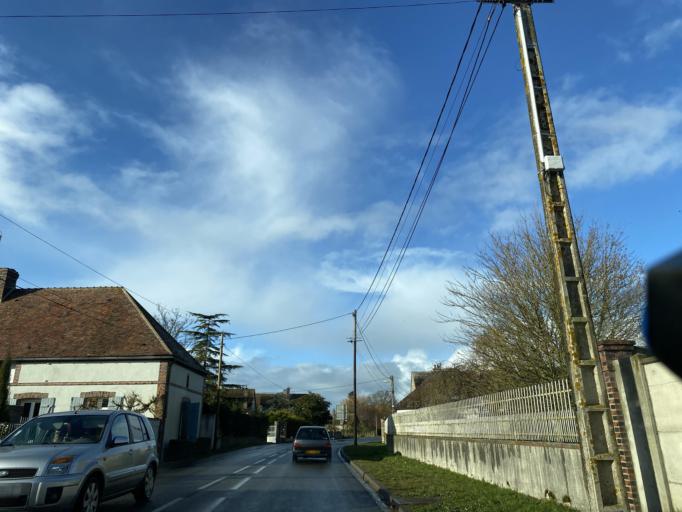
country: FR
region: Centre
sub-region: Departement d'Eure-et-Loir
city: Brezolles
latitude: 48.6531
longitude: 1.1291
